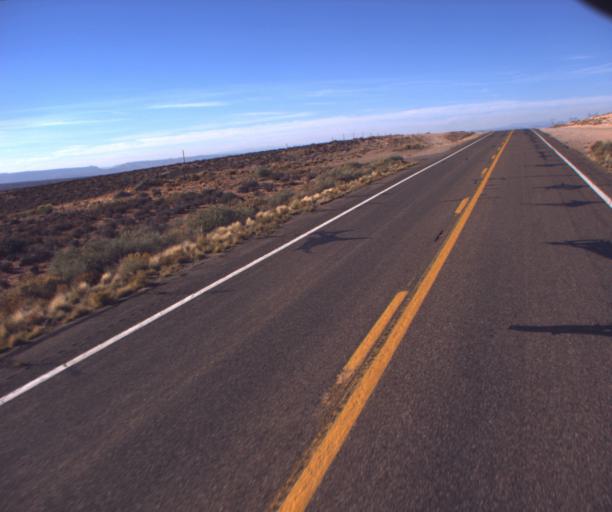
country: US
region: Arizona
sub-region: Coconino County
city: LeChee
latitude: 36.7966
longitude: -111.3002
